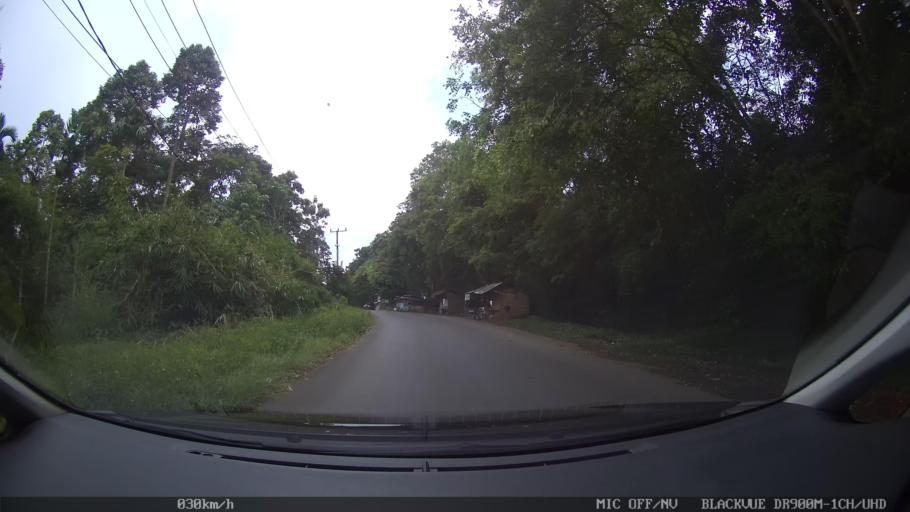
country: ID
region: Lampung
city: Bandarlampung
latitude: -5.4209
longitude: 105.1863
